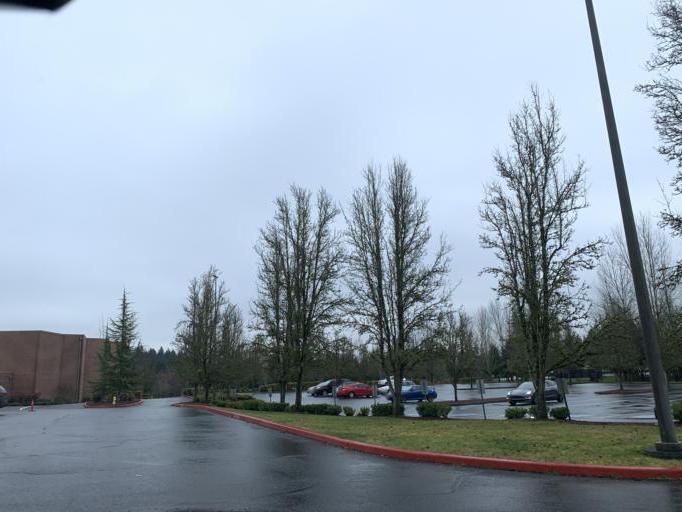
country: US
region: Washington
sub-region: Clark County
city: Barberton
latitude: 45.6806
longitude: -122.5940
